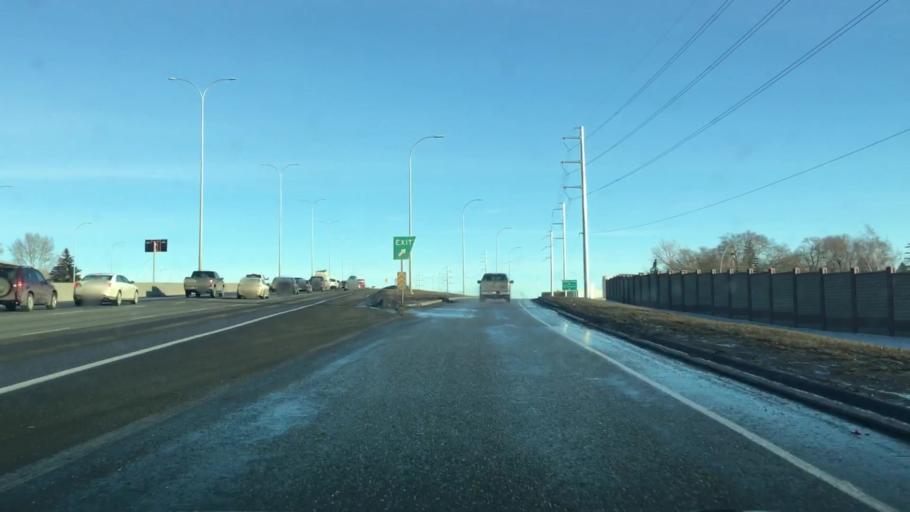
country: CA
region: Alberta
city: Calgary
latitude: 50.9790
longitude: -114.0038
